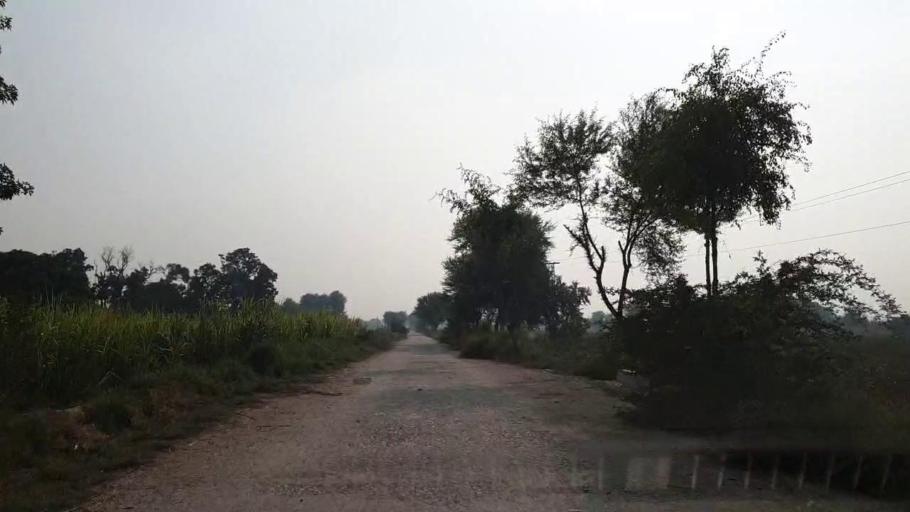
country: PK
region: Sindh
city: Bhan
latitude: 26.5866
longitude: 67.7309
